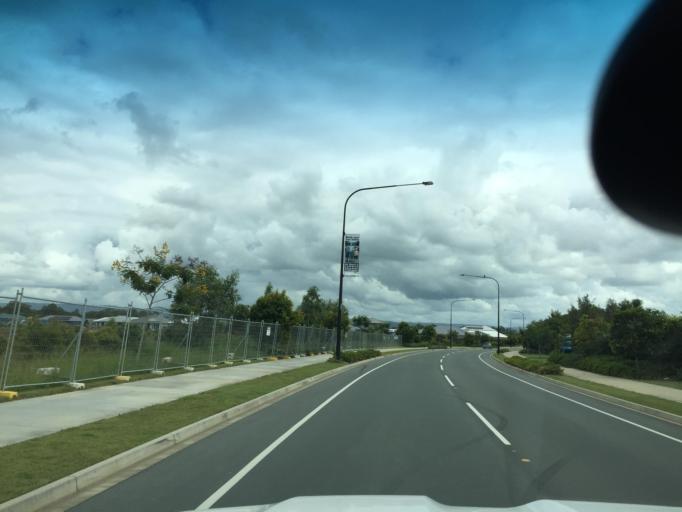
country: AU
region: Queensland
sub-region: Moreton Bay
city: Caboolture South
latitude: -27.0966
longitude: 152.9643
